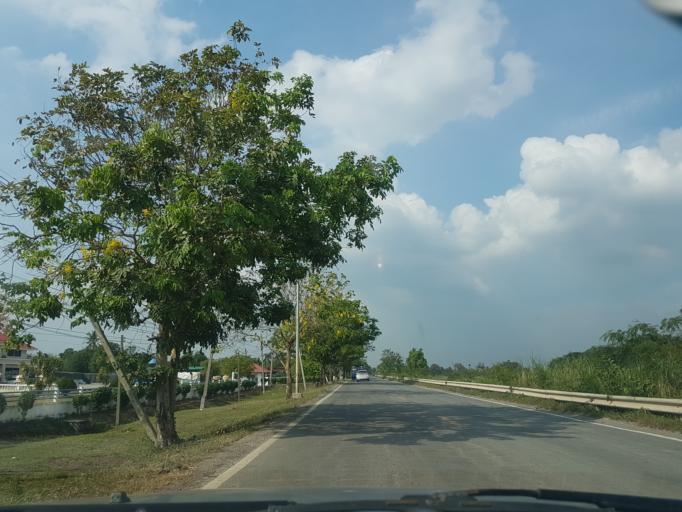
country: TH
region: Phra Nakhon Si Ayutthaya
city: Phachi
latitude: 14.4105
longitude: 100.7845
